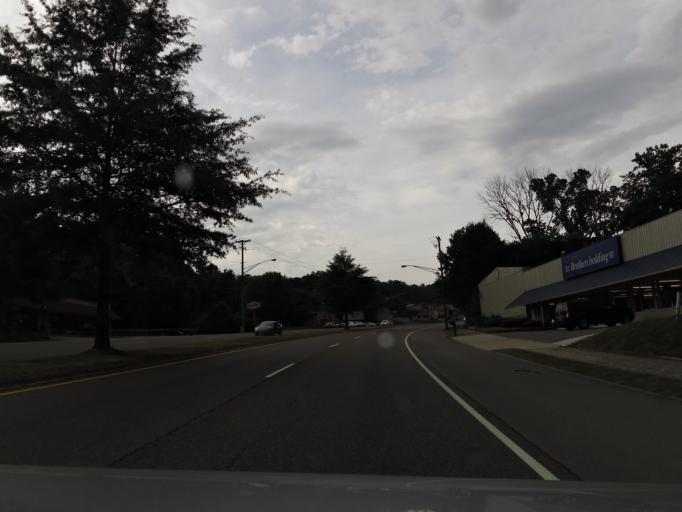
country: US
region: Tennessee
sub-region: Knox County
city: Knoxville
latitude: 36.0451
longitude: -83.9296
